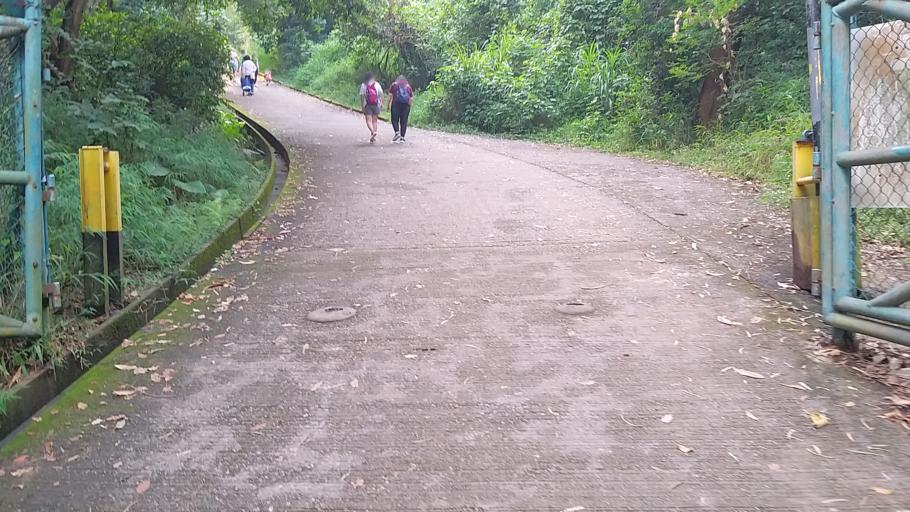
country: HK
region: Tuen Mun
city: Tuen Mun
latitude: 22.4046
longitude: 113.9578
